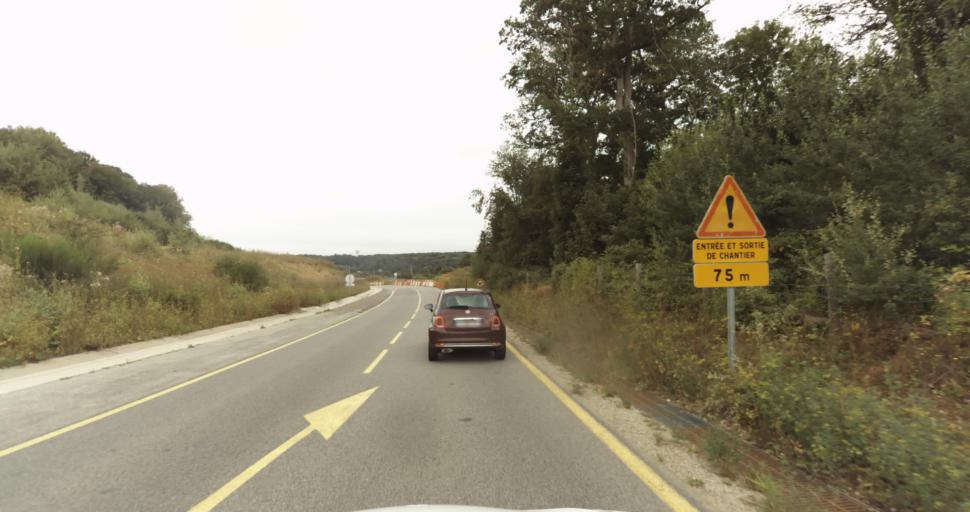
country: FR
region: Haute-Normandie
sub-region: Departement de l'Eure
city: Arnieres-sur-Iton
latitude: 49.0032
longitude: 1.1178
